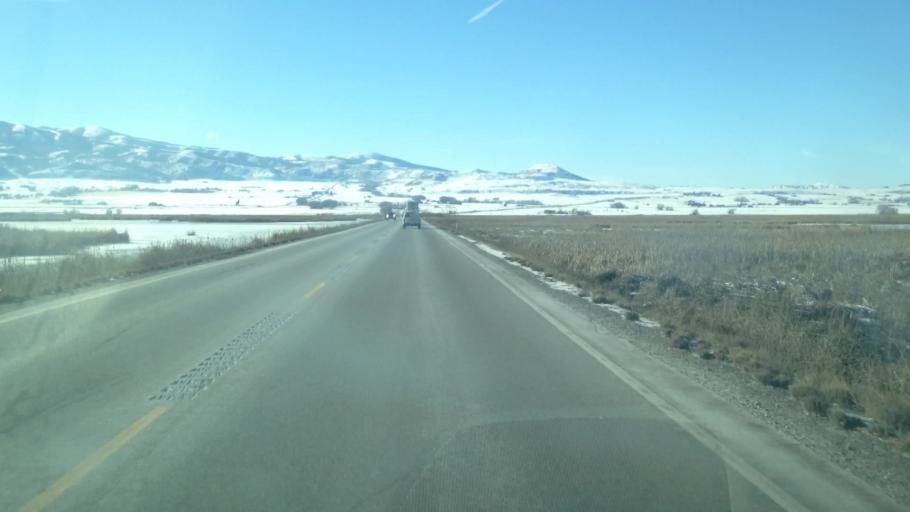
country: US
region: Utah
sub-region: Cache County
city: Benson
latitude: 41.7460
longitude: -111.9409
